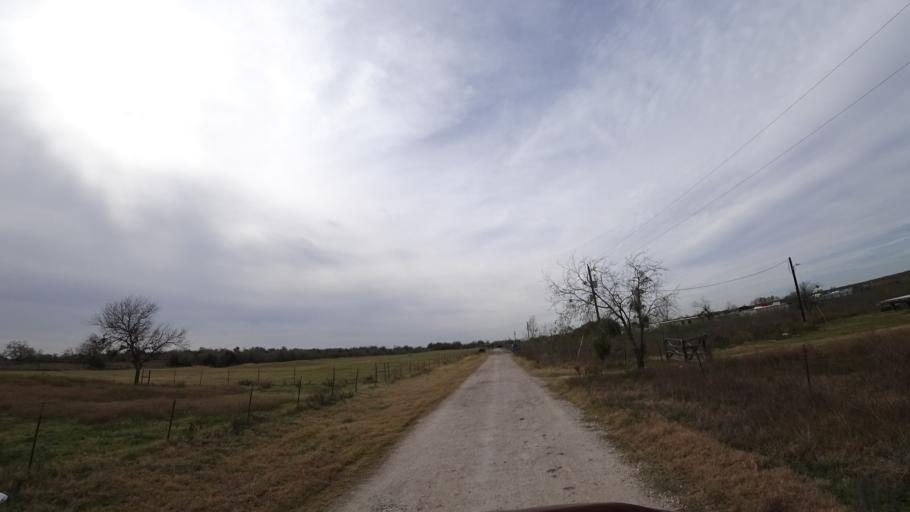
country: US
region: Texas
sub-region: Travis County
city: Garfield
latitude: 30.1145
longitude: -97.5919
